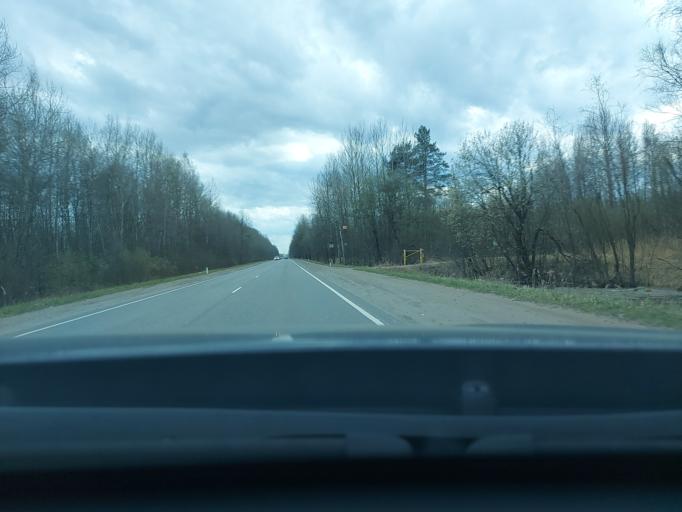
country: RU
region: Leningrad
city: Nikol'skoye
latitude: 59.7456
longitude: 30.7754
